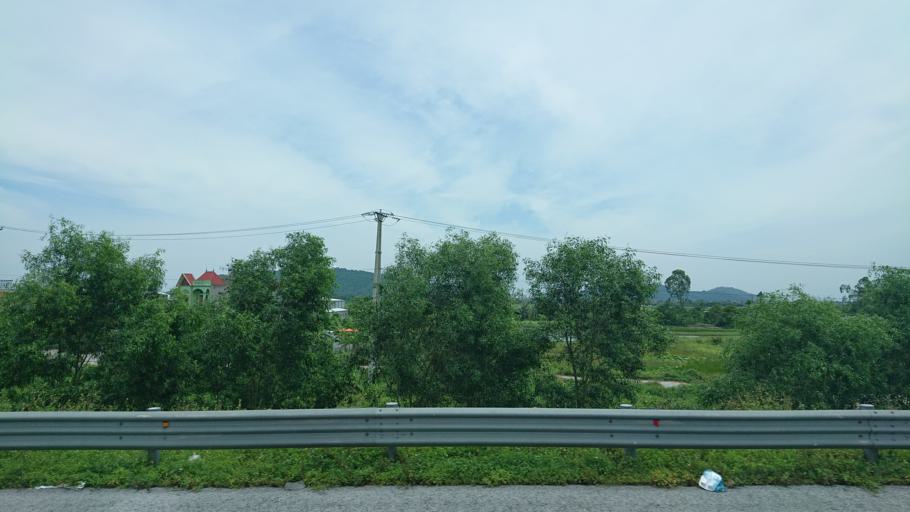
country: VN
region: Hai Phong
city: Nui Doi
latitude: 20.7707
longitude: 106.6185
